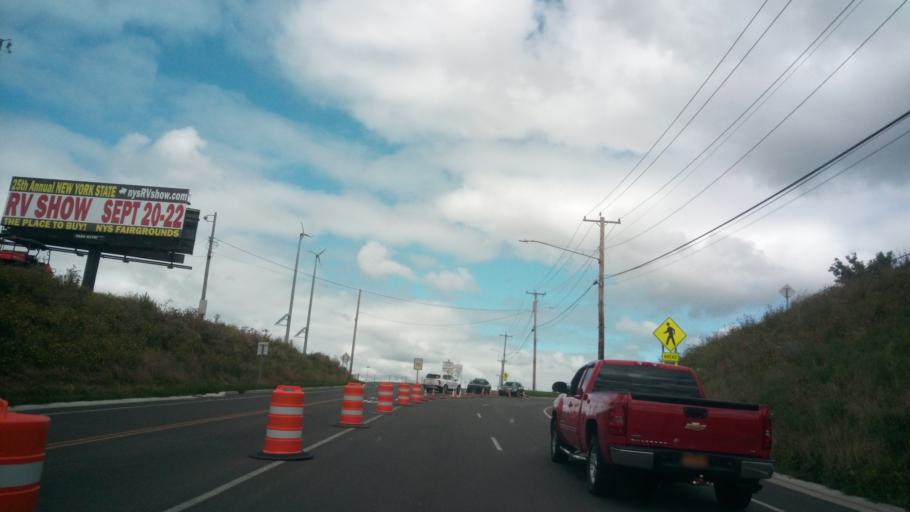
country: US
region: New York
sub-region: Onondaga County
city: Solvay
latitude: 43.0734
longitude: -76.2078
